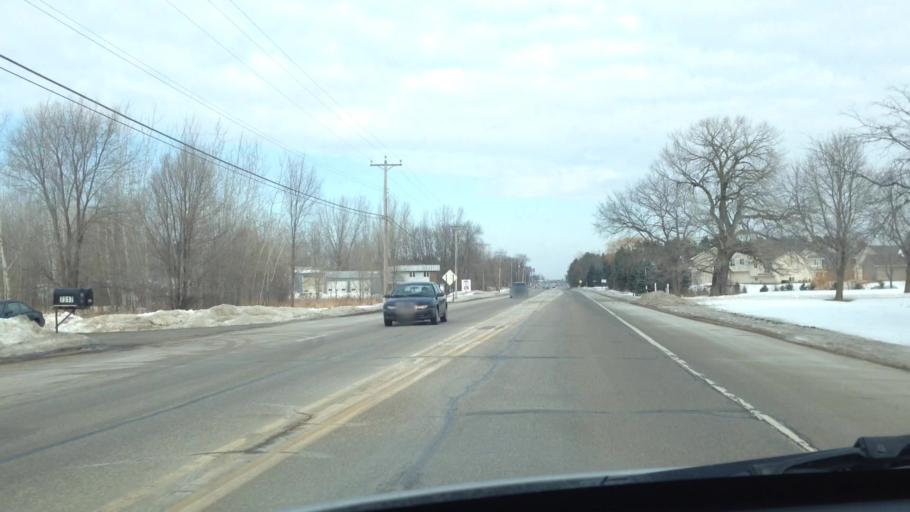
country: US
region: Minnesota
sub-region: Anoka County
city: Lino Lakes
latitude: 45.1702
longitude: -93.1196
